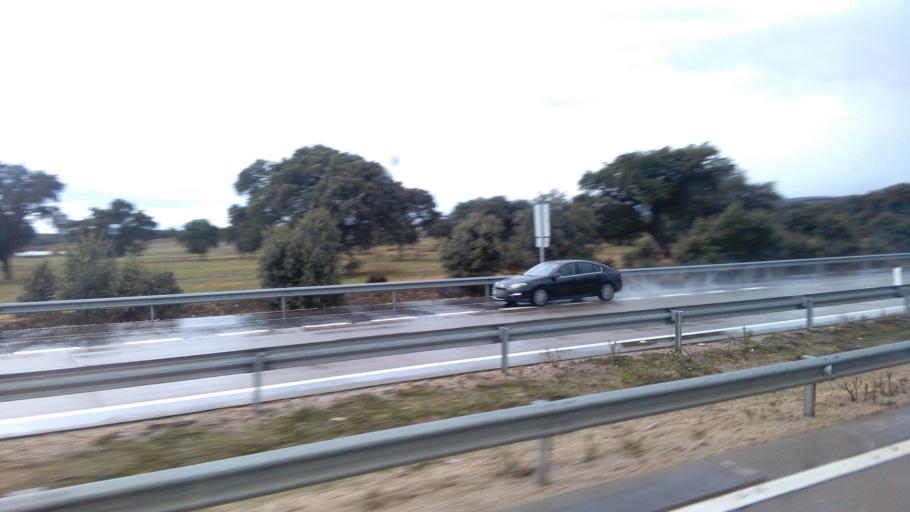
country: ES
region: Castille-La Mancha
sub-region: Province of Toledo
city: Cervera de los Montes
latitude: 40.0138
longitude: -4.7815
